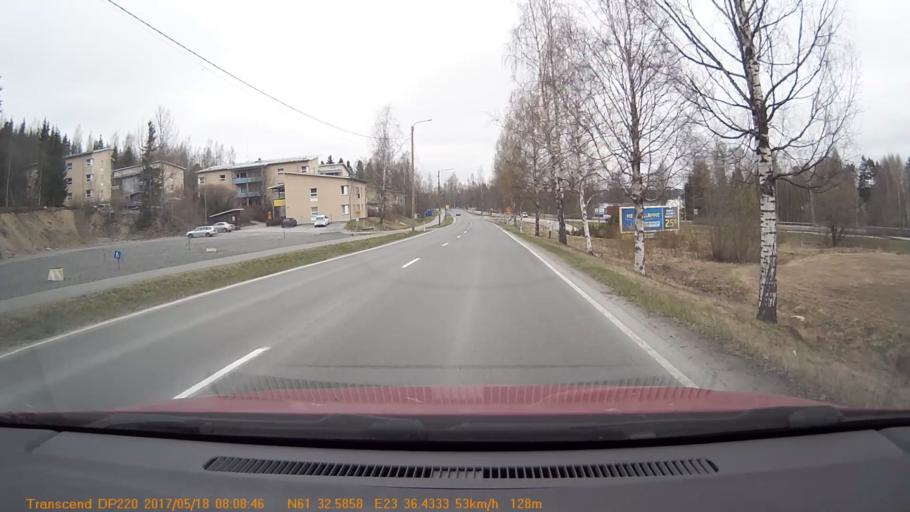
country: FI
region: Pirkanmaa
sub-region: Tampere
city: Yloejaervi
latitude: 61.5443
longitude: 23.6061
